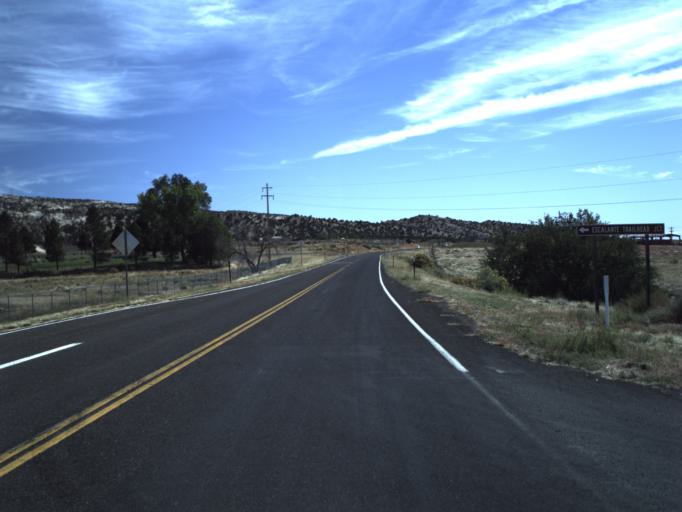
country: US
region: Utah
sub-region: Wayne County
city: Loa
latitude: 37.7648
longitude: -111.5861
